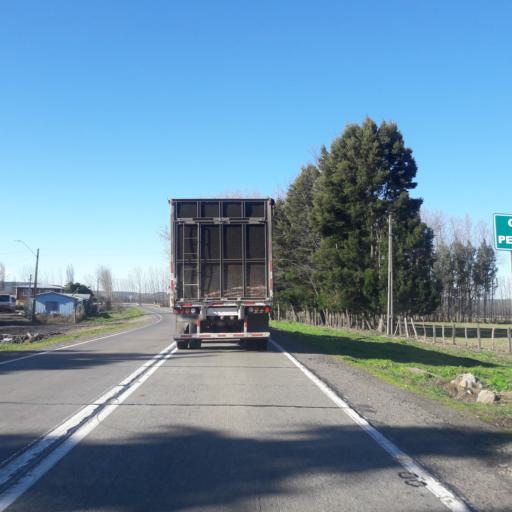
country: CL
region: Araucania
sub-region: Provincia de Malleco
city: Angol
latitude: -37.7838
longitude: -72.5286
